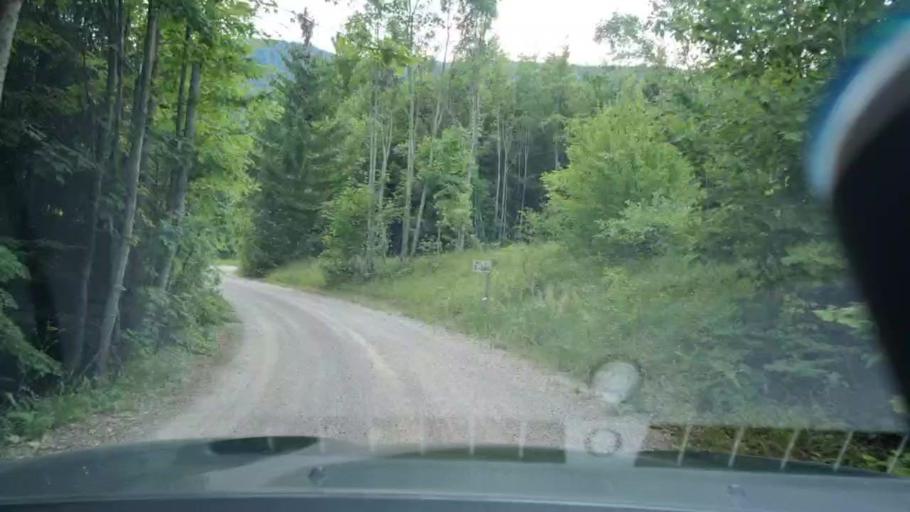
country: BA
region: Federation of Bosnia and Herzegovina
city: Bosansko Grahovo
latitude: 44.3184
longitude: 16.2468
